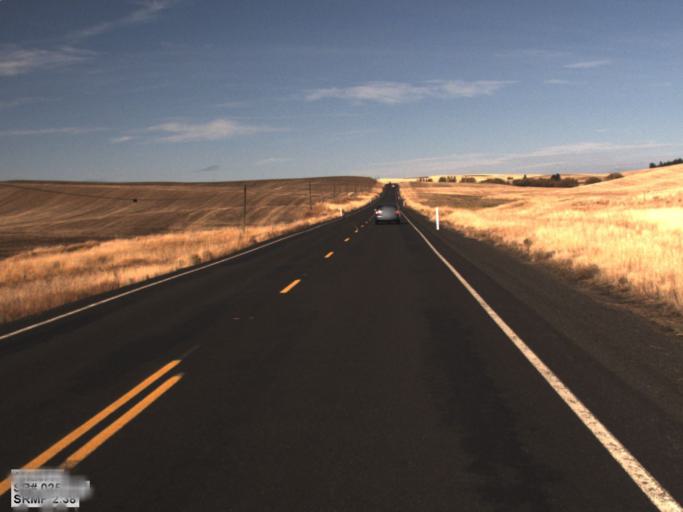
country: US
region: Washington
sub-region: Lincoln County
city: Davenport
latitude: 47.6893
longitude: -118.1410
